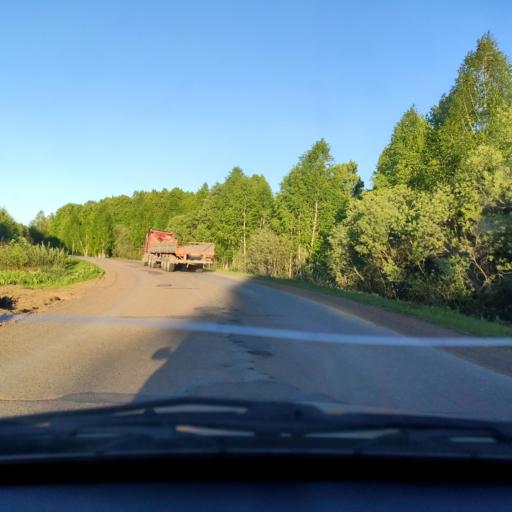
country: RU
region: Bashkortostan
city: Blagoveshchensk
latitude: 55.0317
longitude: 56.0979
